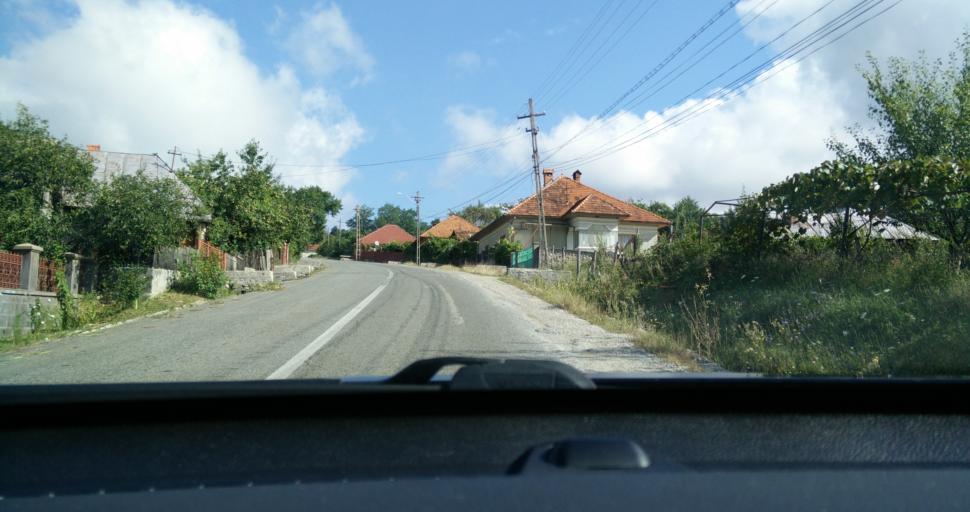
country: RO
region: Gorj
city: Novaci-Straini
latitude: 45.1820
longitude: 23.6820
